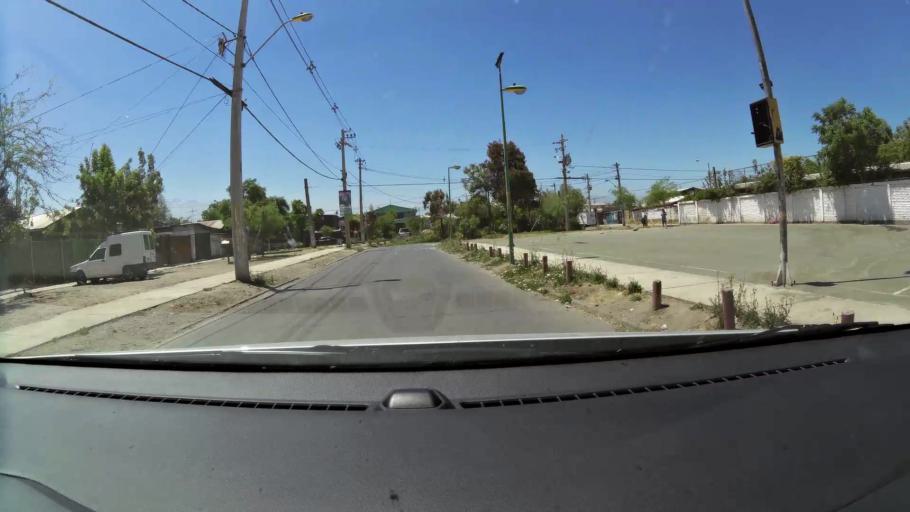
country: CL
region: Santiago Metropolitan
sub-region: Provincia de Santiago
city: La Pintana
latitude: -33.5666
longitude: -70.6599
